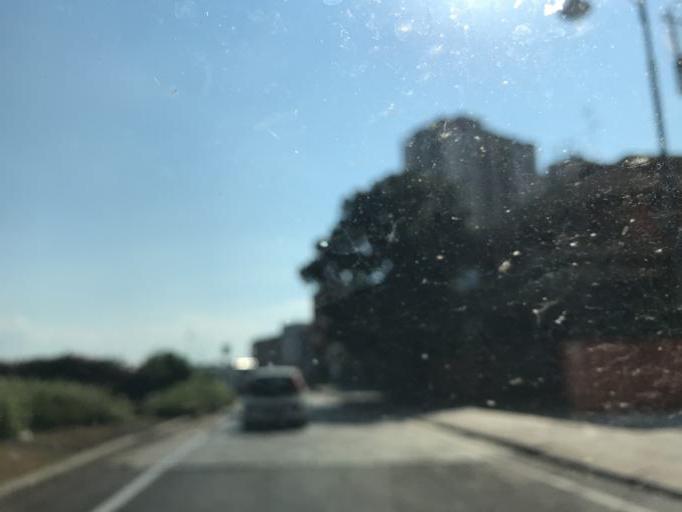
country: IT
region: Sardinia
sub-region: Provincia di Olbia-Tempio
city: Olbia
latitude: 40.9222
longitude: 9.5041
